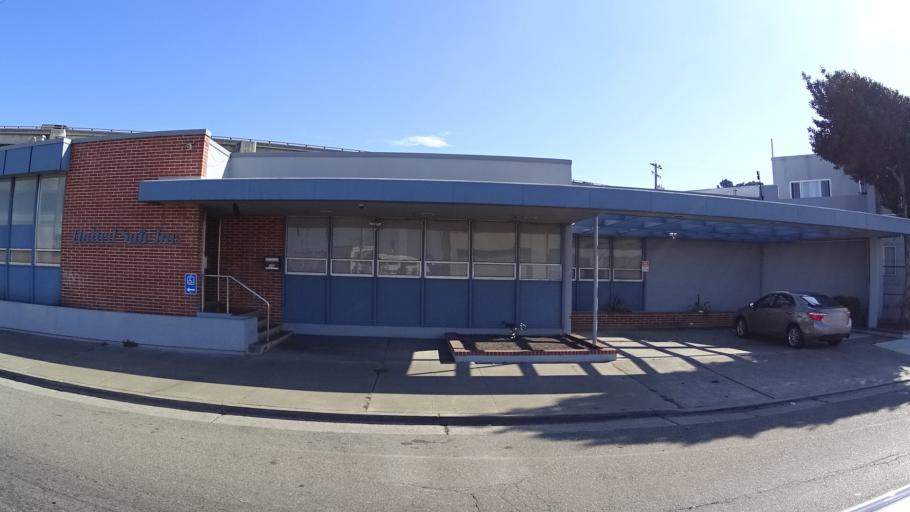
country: US
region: California
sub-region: San Francisco County
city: San Francisco
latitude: 37.7395
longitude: -122.4012
